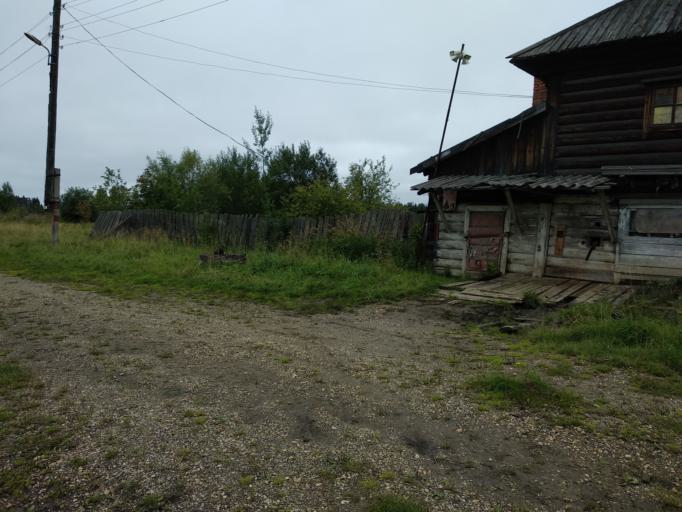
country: RU
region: Sverdlovsk
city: Serov
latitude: 59.8427
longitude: 60.7281
